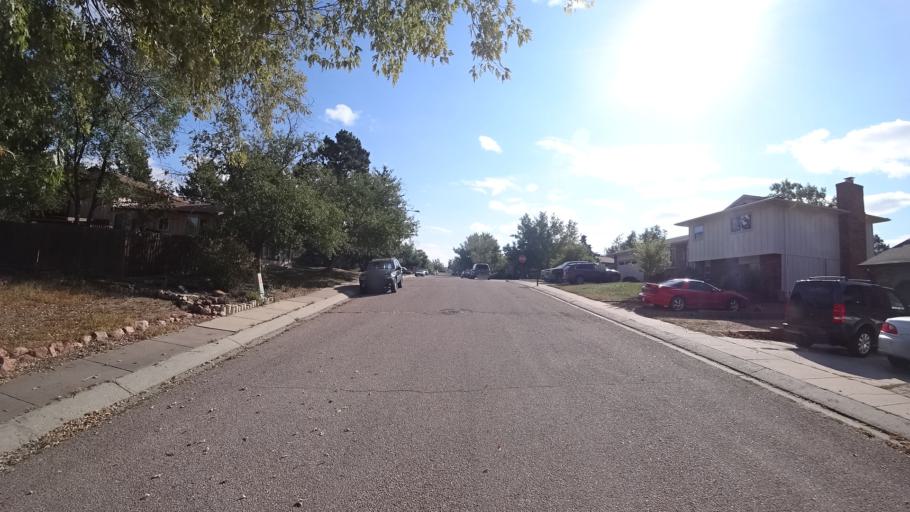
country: US
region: Colorado
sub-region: El Paso County
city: Cimarron Hills
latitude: 38.8828
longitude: -104.7319
